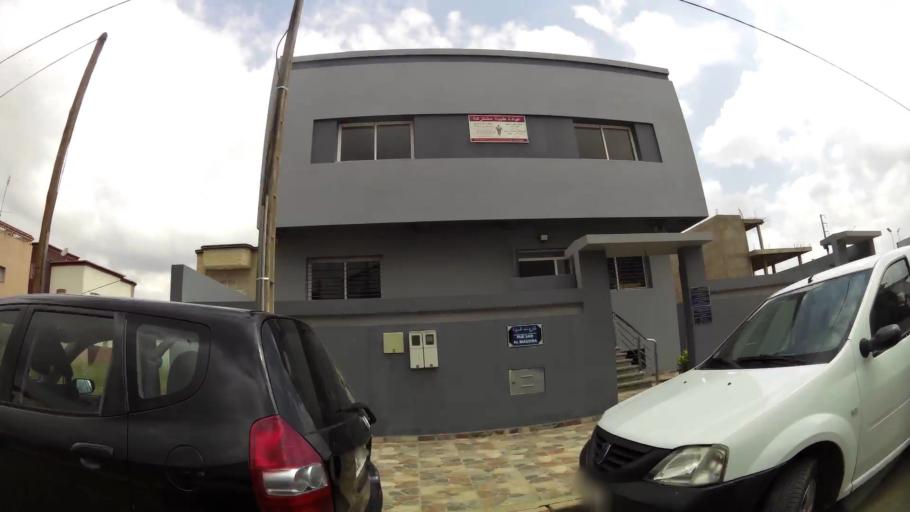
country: MA
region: Rabat-Sale-Zemmour-Zaer
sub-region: Khemisset
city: Tiflet
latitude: 33.8933
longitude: -6.3305
